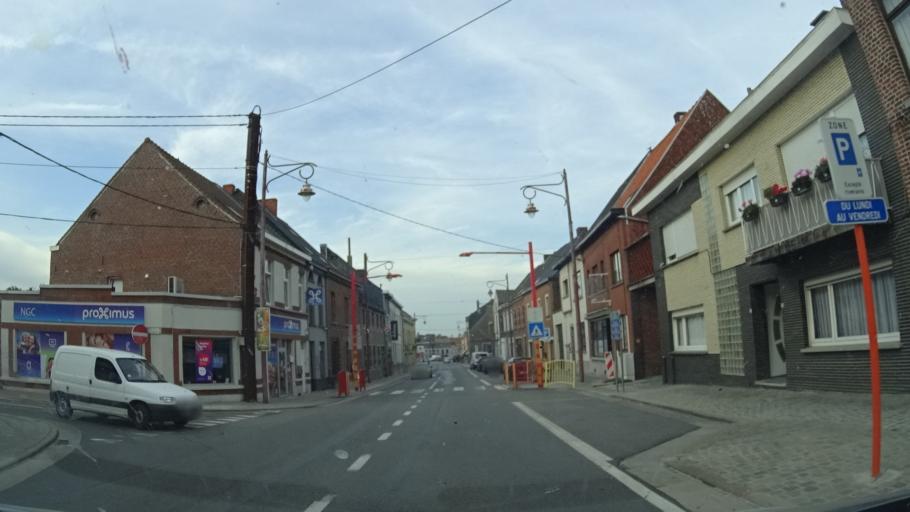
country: BE
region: Wallonia
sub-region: Province du Hainaut
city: Frasnes-lez-Buissenal
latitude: 50.5962
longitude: 3.6177
